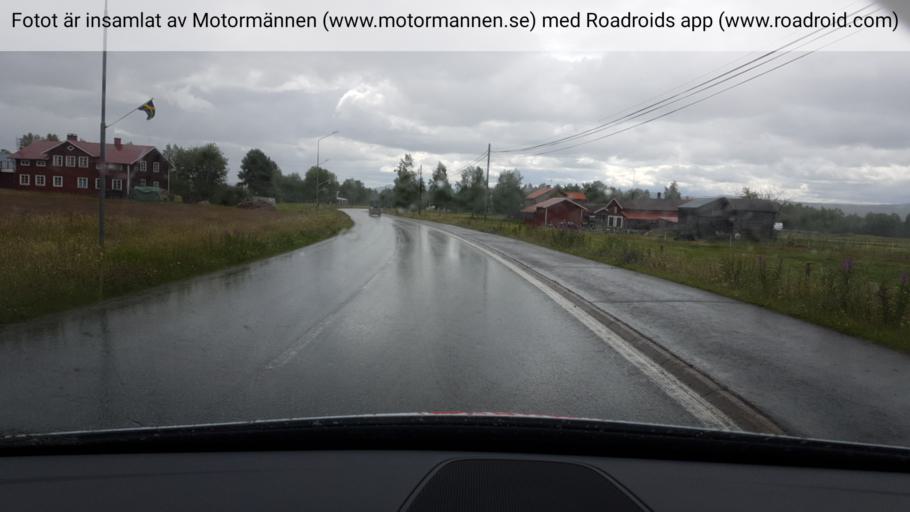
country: SE
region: Jaemtland
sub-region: Harjedalens Kommun
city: Sveg
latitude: 62.4547
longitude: 13.8630
